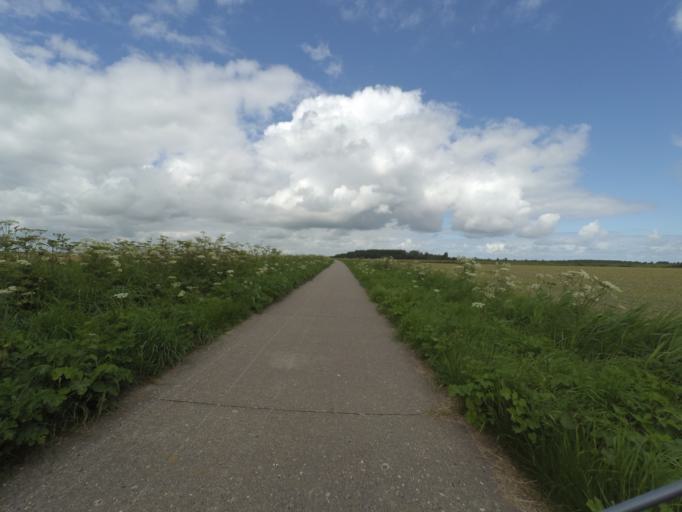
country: NL
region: Groningen
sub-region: Gemeente Zuidhorn
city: Grijpskerk
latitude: 53.3192
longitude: 6.2505
